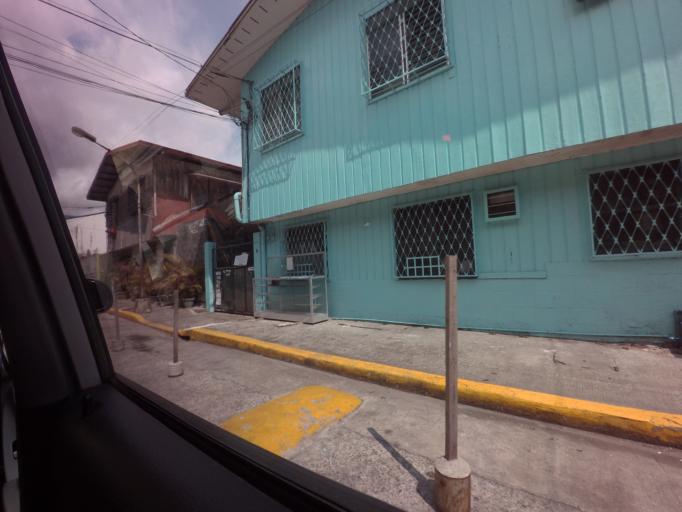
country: PH
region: Metro Manila
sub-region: City of Manila
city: Quiapo
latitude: 14.6003
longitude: 121.0067
